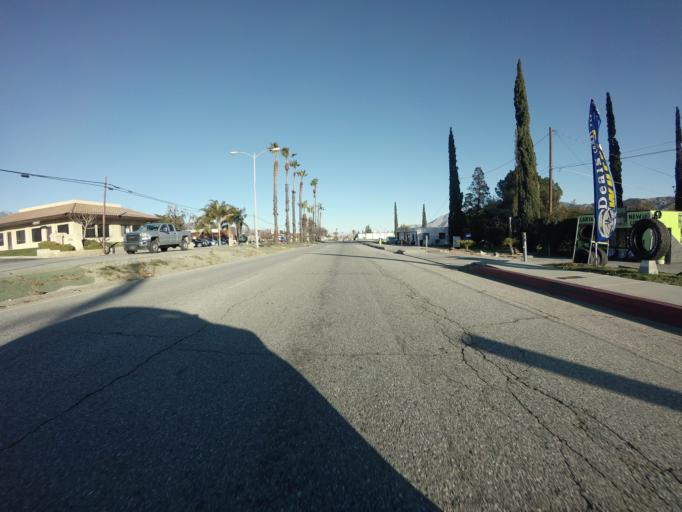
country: US
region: California
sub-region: Riverside County
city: Banning
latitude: 33.9257
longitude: -116.9037
